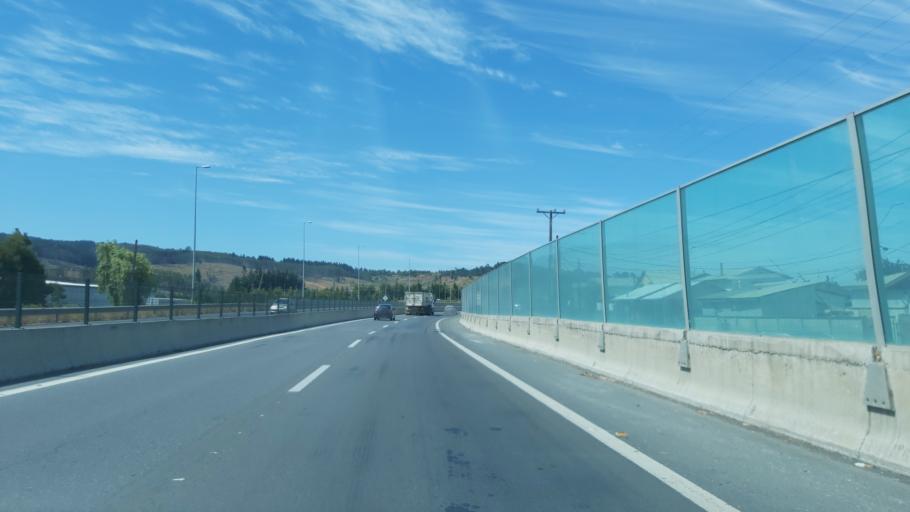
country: CL
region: Biobio
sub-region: Provincia de Concepcion
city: Coronel
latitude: -37.0375
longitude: -73.1349
